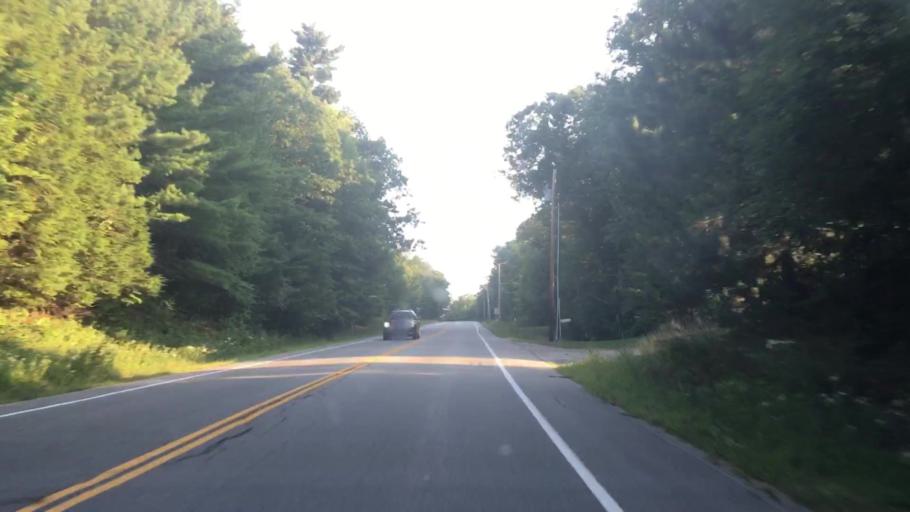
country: US
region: New Hampshire
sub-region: Belknap County
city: Gilmanton
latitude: 43.4436
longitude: -71.4188
